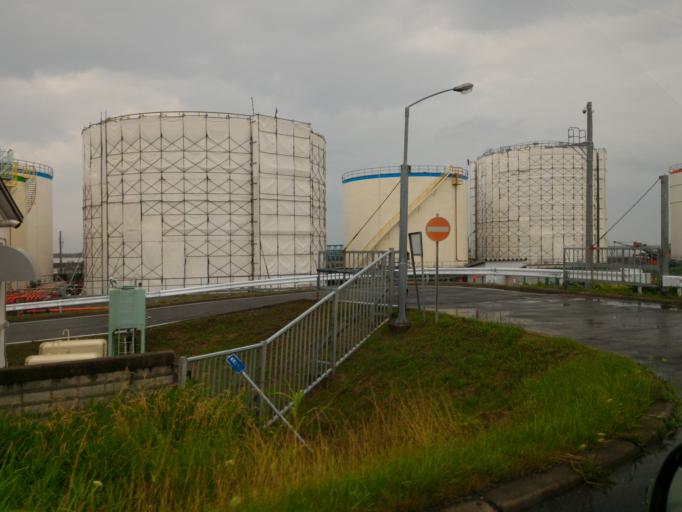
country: JP
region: Hokkaido
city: Rumoi
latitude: 43.9583
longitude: 141.6441
